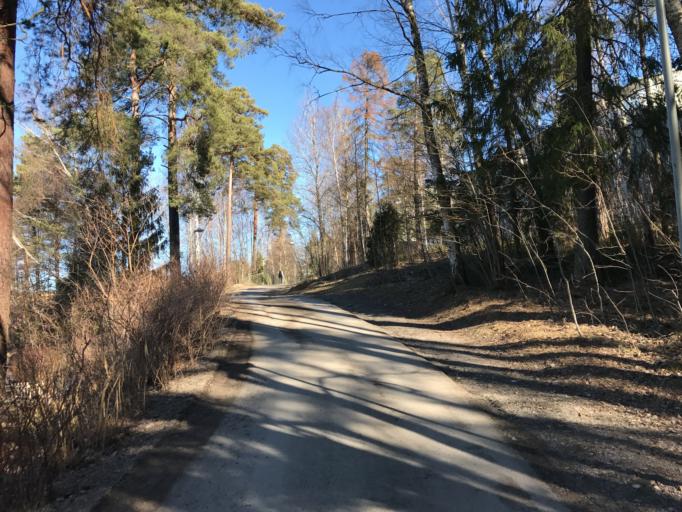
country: SE
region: Stockholm
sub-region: Stockholms Kommun
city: Kista
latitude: 59.4091
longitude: 17.9177
